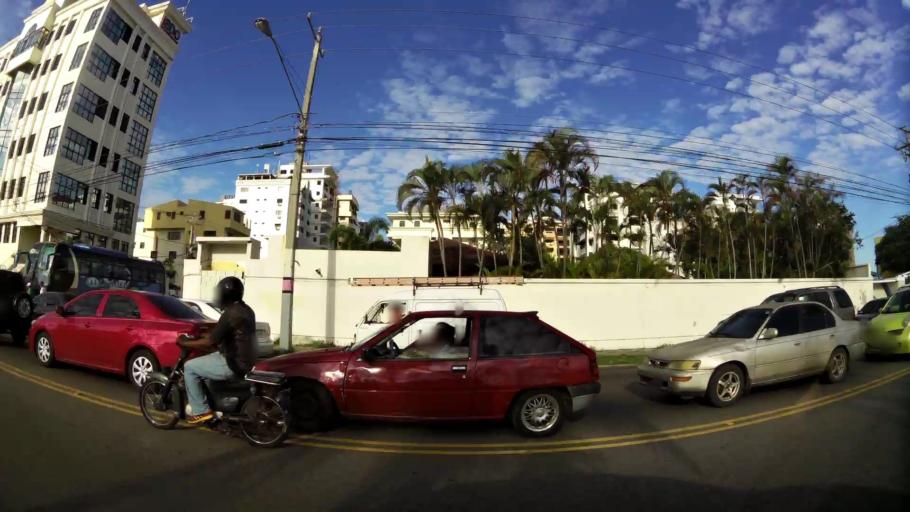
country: DO
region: Nacional
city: La Julia
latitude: 18.4789
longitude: -69.9207
